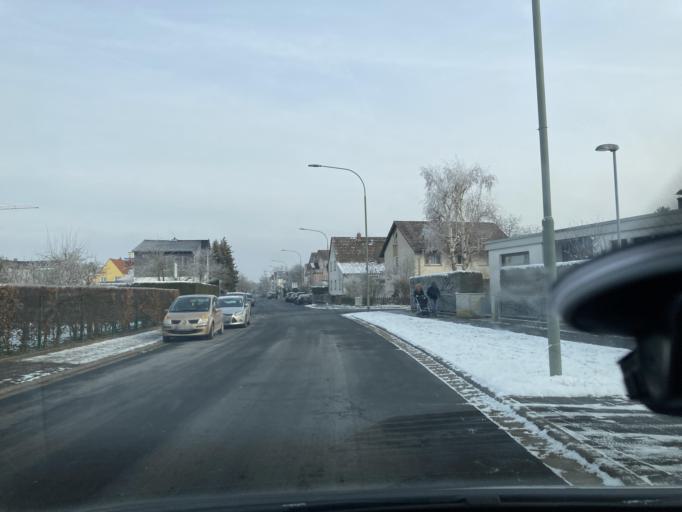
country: DE
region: Hesse
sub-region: Regierungsbezirk Darmstadt
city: Muehlheim am Main
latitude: 50.1082
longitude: 8.8323
